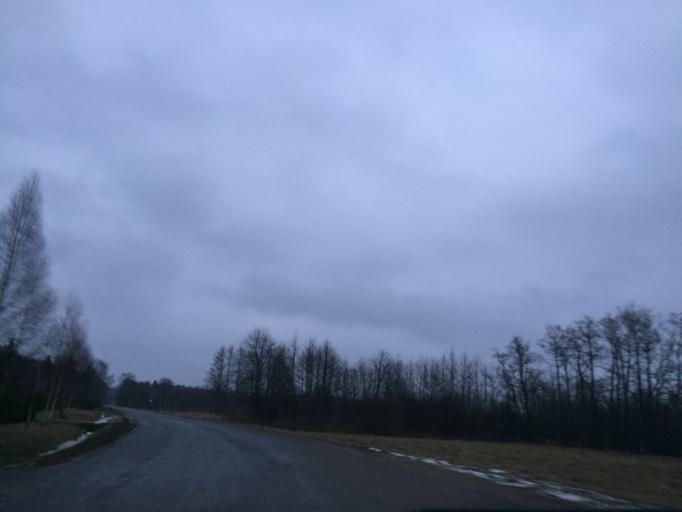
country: EE
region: Saare
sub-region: Kuressaare linn
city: Kuressaare
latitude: 58.5752
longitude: 22.6457
